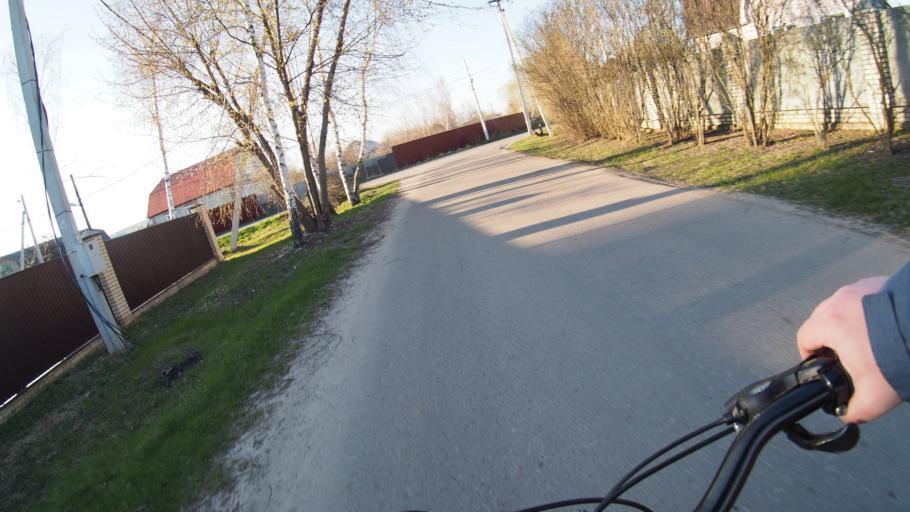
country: RU
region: Moskovskaya
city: Malyshevo
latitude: 55.4976
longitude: 38.3494
